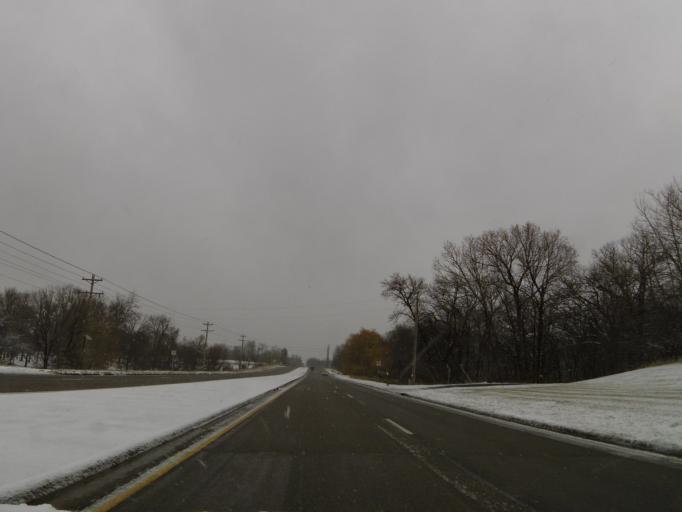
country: US
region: Minnesota
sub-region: Scott County
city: Prior Lake
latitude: 44.7501
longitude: -93.4091
